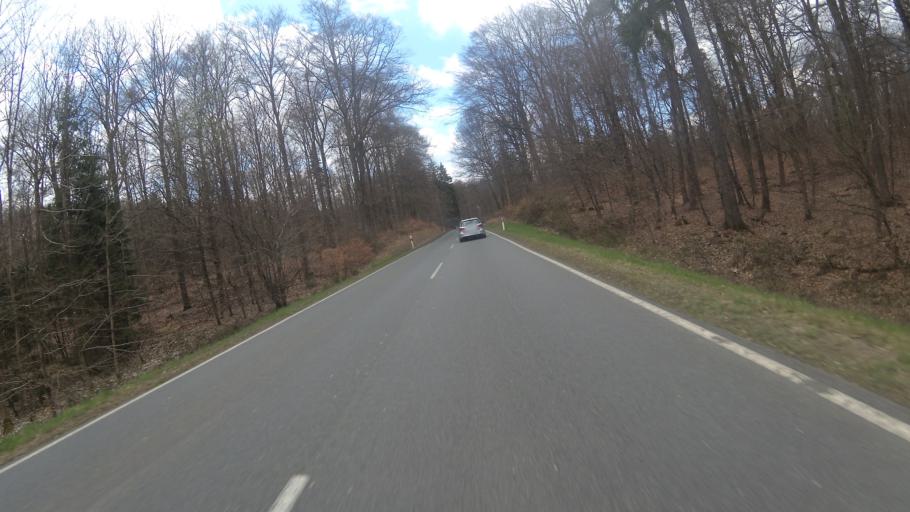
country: DE
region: Rheinland-Pfalz
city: Niederofflingen
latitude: 50.0729
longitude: 6.8830
